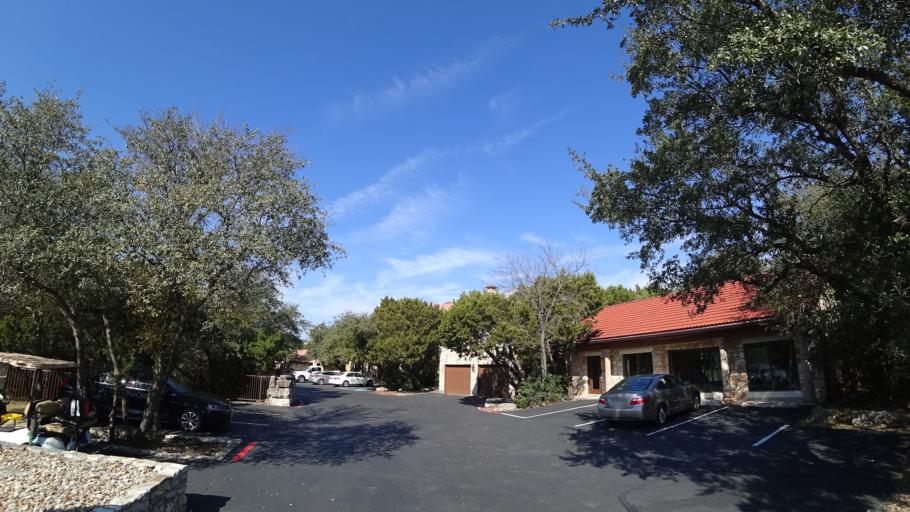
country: US
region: Texas
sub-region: Williamson County
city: Jollyville
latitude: 30.3723
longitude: -97.7615
